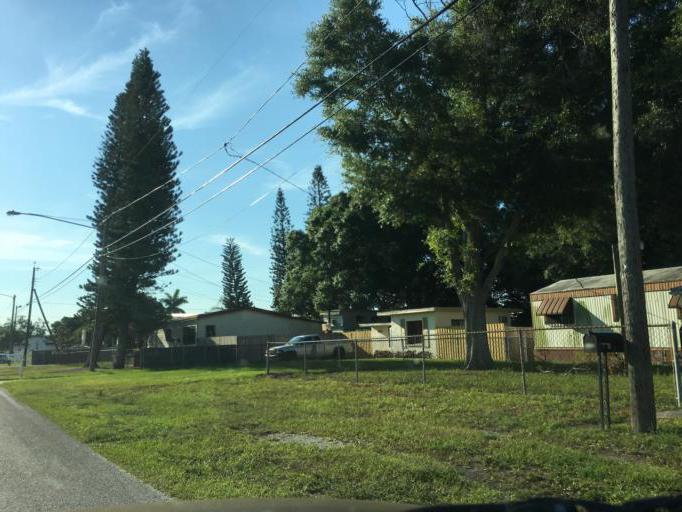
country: US
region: Florida
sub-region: Pinellas County
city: Pinellas Park
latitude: 27.8338
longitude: -82.7018
